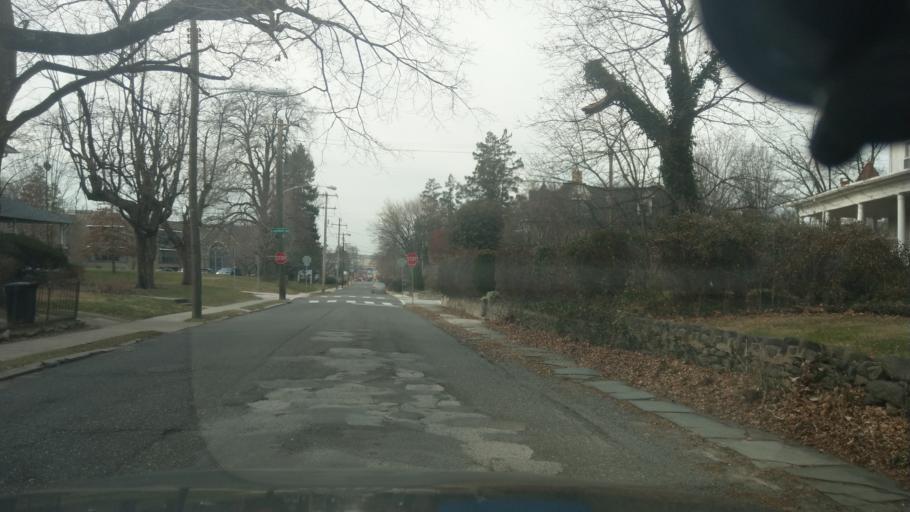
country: US
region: Pennsylvania
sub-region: Montgomery County
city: Jenkintown
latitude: 40.0552
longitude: -75.1341
